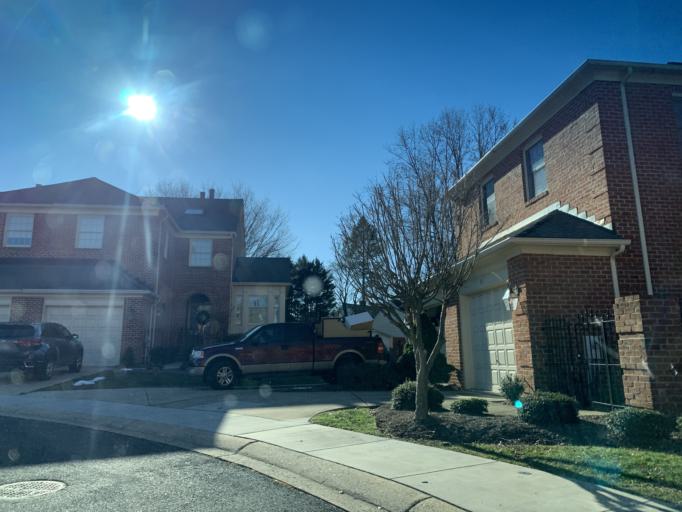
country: US
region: Maryland
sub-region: Harford County
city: North Bel Air
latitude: 39.5433
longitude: -76.3502
